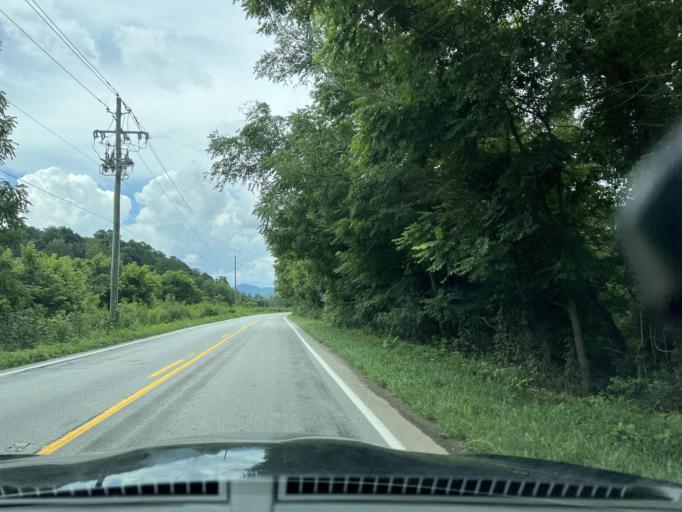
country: US
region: North Carolina
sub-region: Henderson County
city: Hoopers Creek
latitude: 35.4488
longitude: -82.4776
